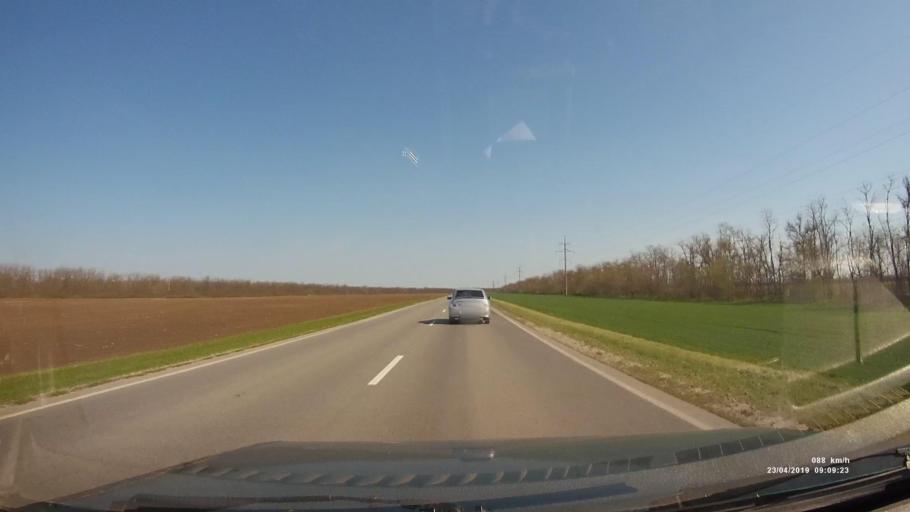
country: RU
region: Rostov
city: Sal'sk
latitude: 46.5731
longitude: 41.6138
